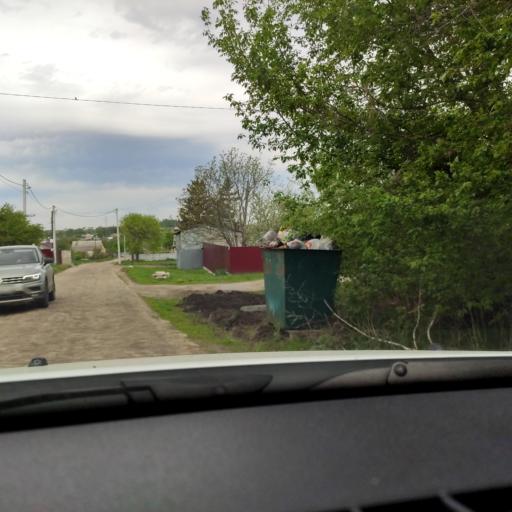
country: RU
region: Voronezj
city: Devitsa
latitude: 51.6410
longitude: 38.9564
